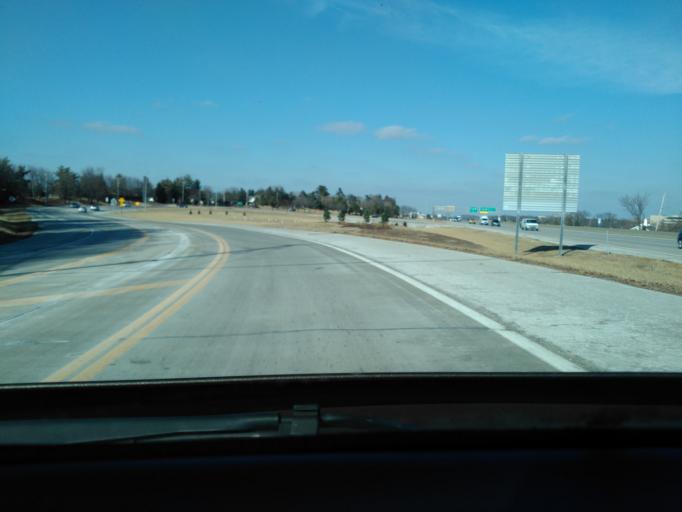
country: US
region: Missouri
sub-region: Saint Louis County
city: Manchester
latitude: 38.6327
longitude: -90.5140
